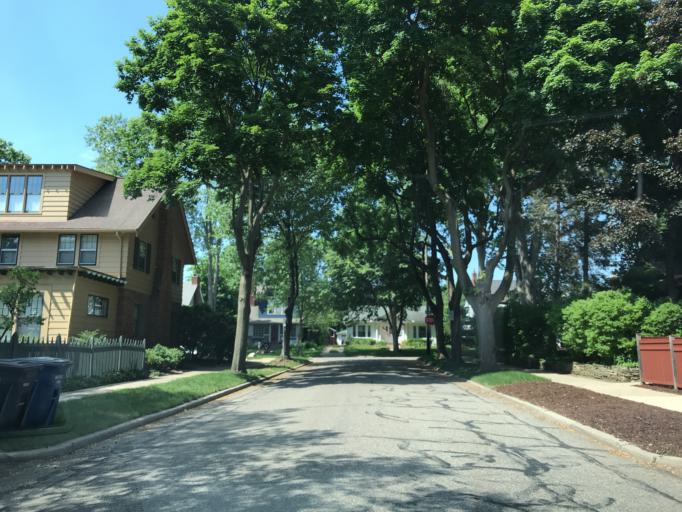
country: US
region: Michigan
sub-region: Washtenaw County
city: Ann Arbor
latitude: 42.2640
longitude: -83.7277
